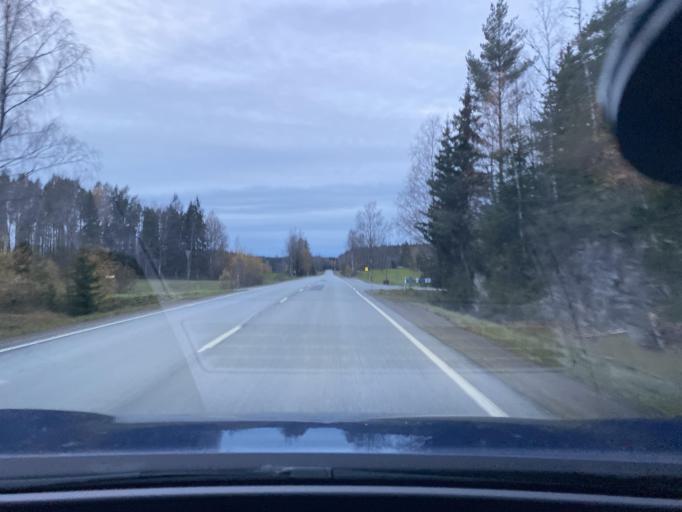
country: FI
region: Uusimaa
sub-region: Helsinki
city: Sammatti
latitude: 60.3873
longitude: 23.8308
